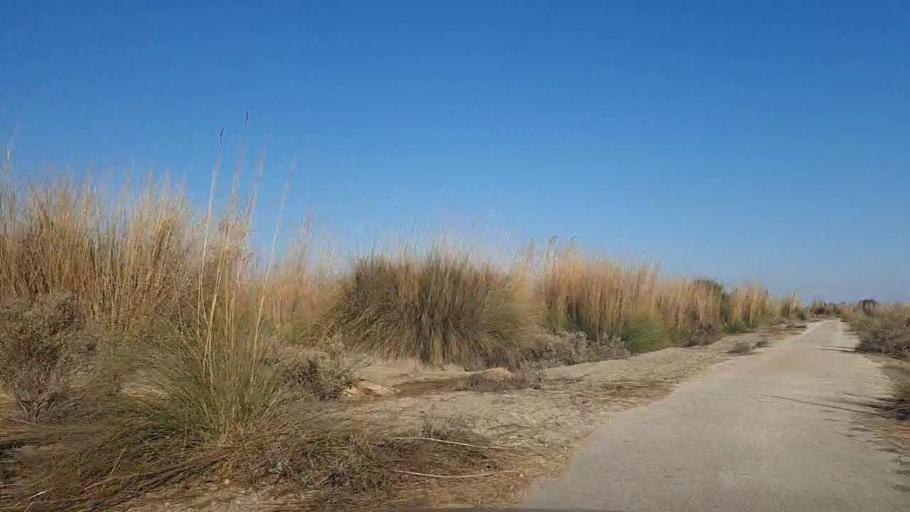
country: PK
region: Sindh
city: Khadro
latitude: 26.2498
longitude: 68.8643
